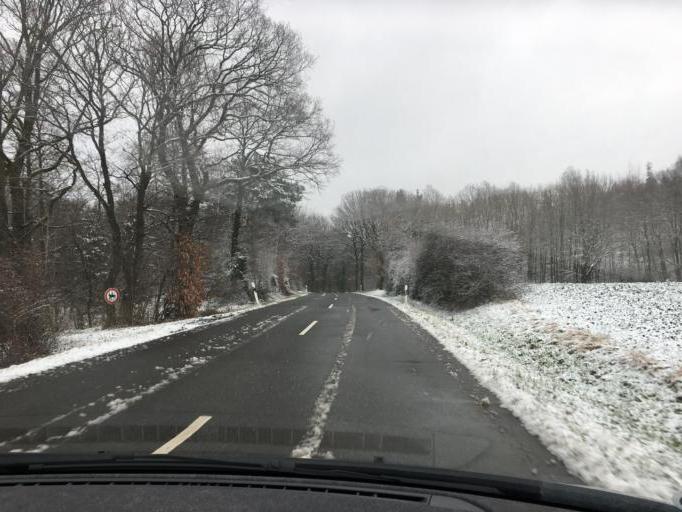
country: DE
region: North Rhine-Westphalia
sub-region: Regierungsbezirk Koln
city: Kreuzau
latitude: 50.7386
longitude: 6.4432
